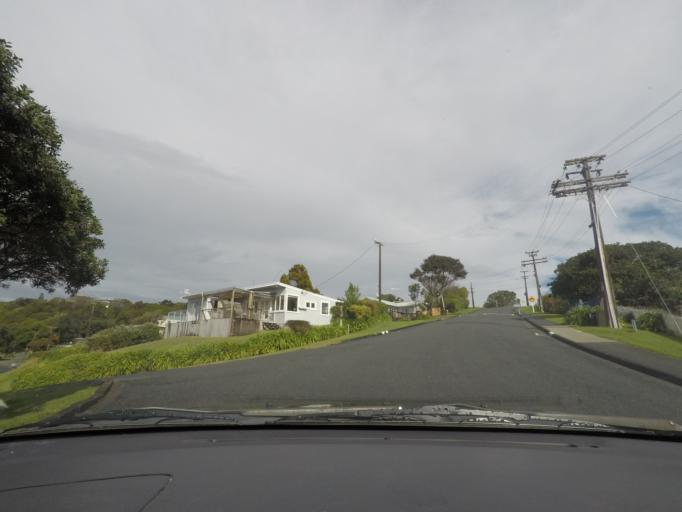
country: NZ
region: Auckland
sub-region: Auckland
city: Warkworth
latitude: -36.4228
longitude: 174.7309
